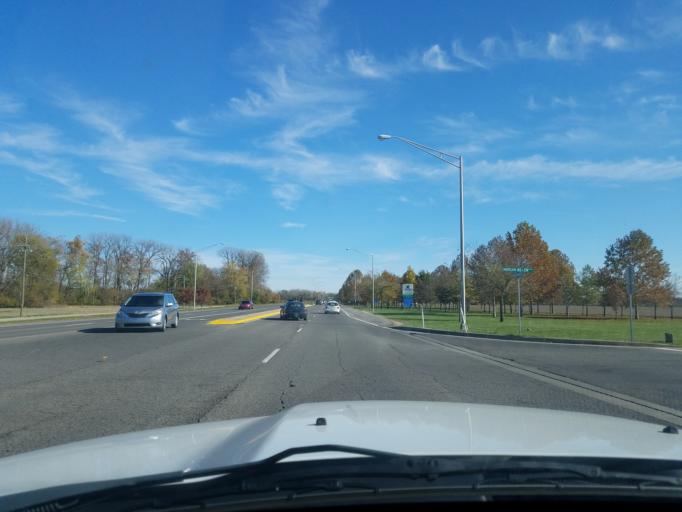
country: US
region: Indiana
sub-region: Bartholomew County
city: Columbus
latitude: 39.2000
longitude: -85.9449
